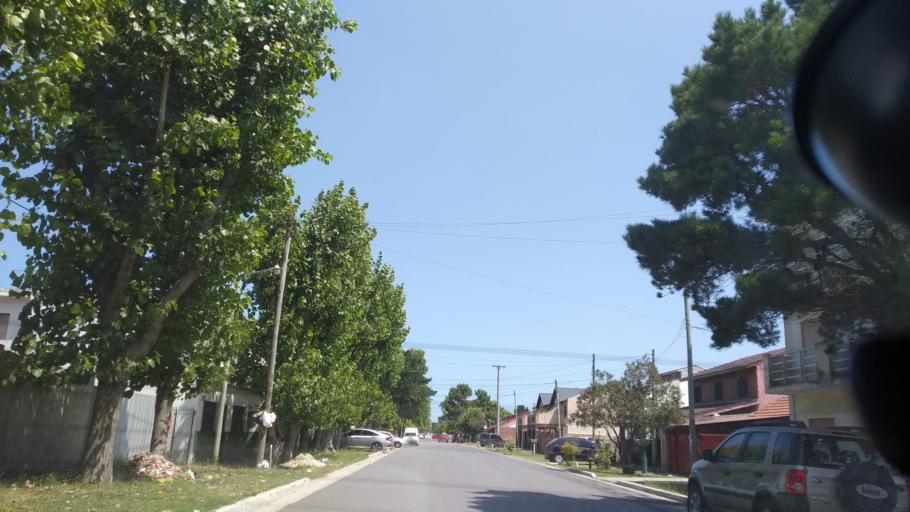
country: AR
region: Buenos Aires
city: Mar del Tuyu
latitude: -36.5784
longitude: -56.6936
